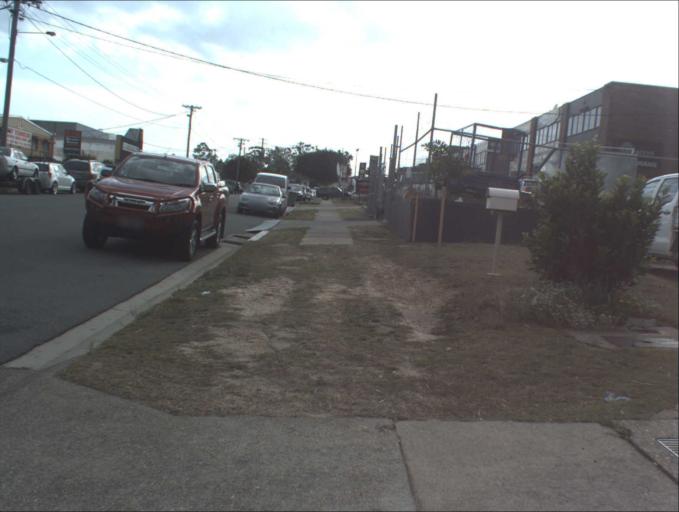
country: AU
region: Queensland
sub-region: Logan
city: Springwood
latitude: -27.6255
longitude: 153.1198
